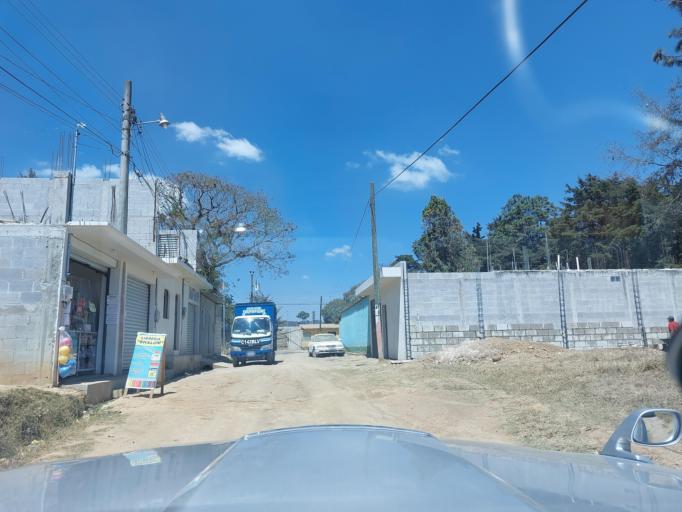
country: GT
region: Chimaltenango
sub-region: Municipio de Chimaltenango
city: Chimaltenango
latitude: 14.6543
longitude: -90.8266
